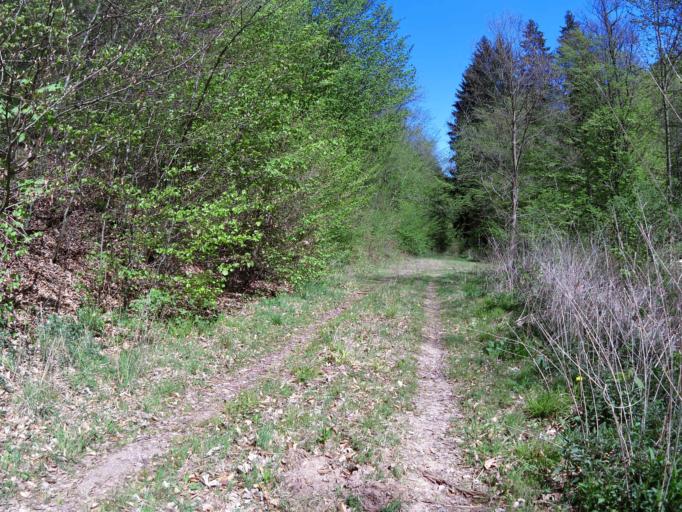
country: DE
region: Thuringia
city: Wolfsburg-Unkeroda
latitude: 50.9701
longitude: 10.2655
